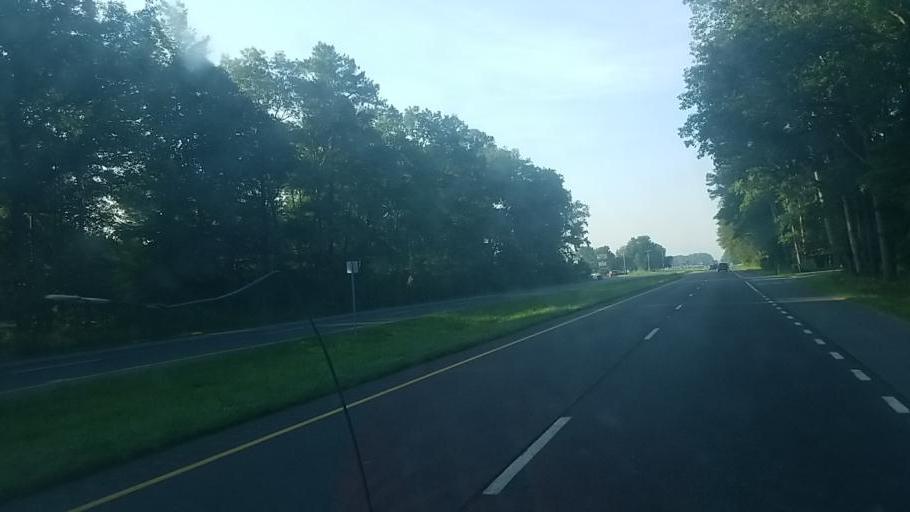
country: US
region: Delaware
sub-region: Sussex County
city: Selbyville
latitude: 38.4859
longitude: -75.2360
